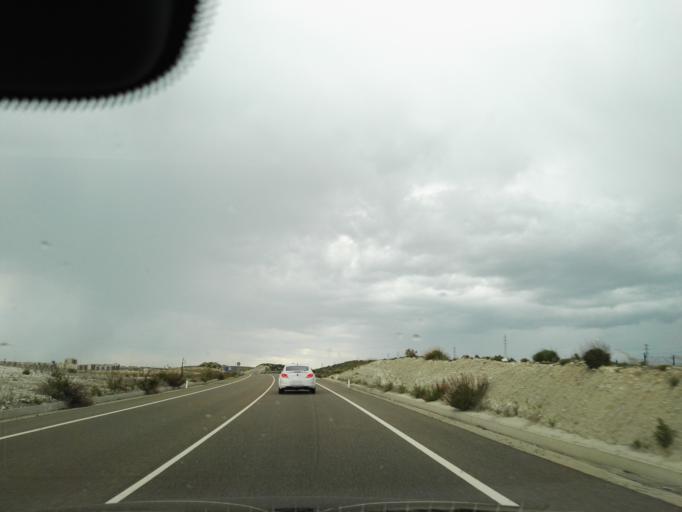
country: ES
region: Aragon
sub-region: Provincia de Zaragoza
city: Montecanal
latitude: 41.6223
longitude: -0.9805
